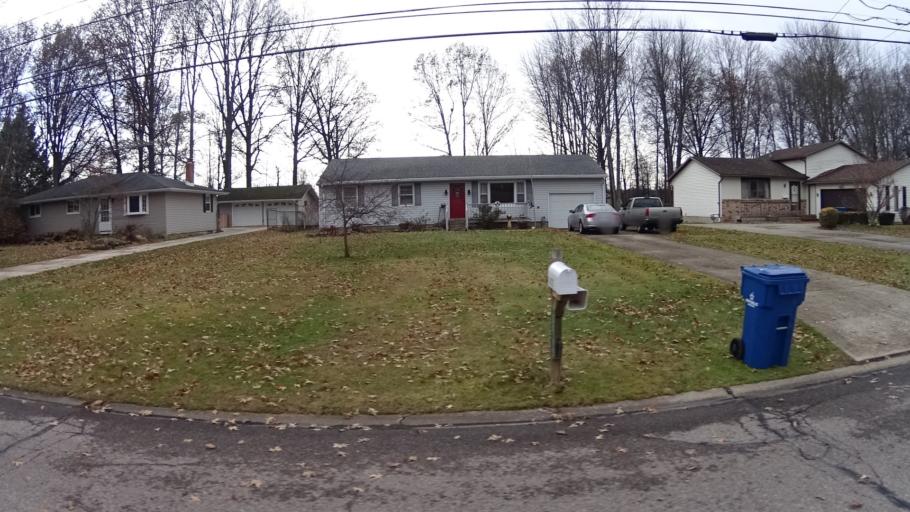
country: US
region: Ohio
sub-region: Lorain County
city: North Ridgeville
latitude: 41.3702
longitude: -82.0214
